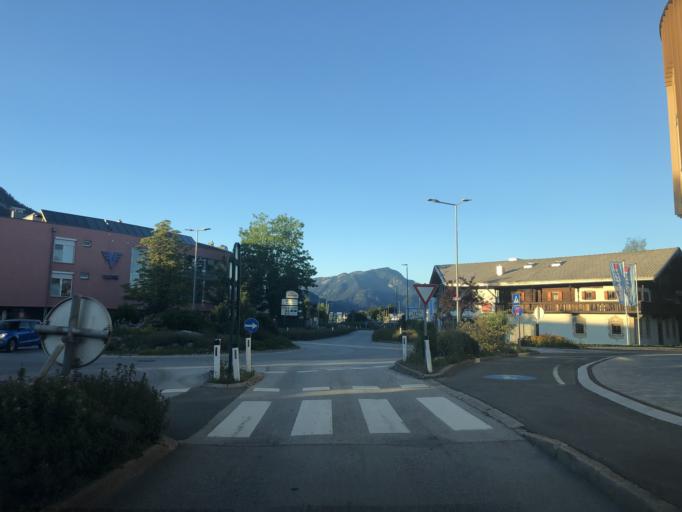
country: AT
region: Tyrol
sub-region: Politischer Bezirk Kitzbuhel
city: Sankt Johann in Tirol
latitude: 47.5229
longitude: 12.4213
